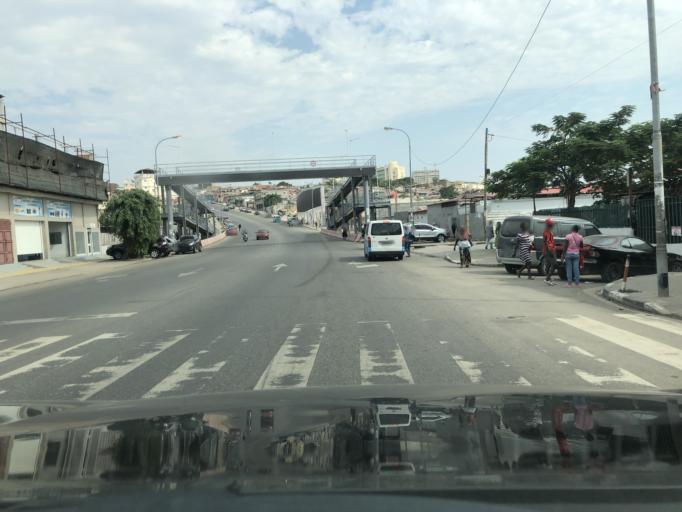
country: AO
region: Luanda
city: Luanda
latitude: -8.8289
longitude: 13.2261
